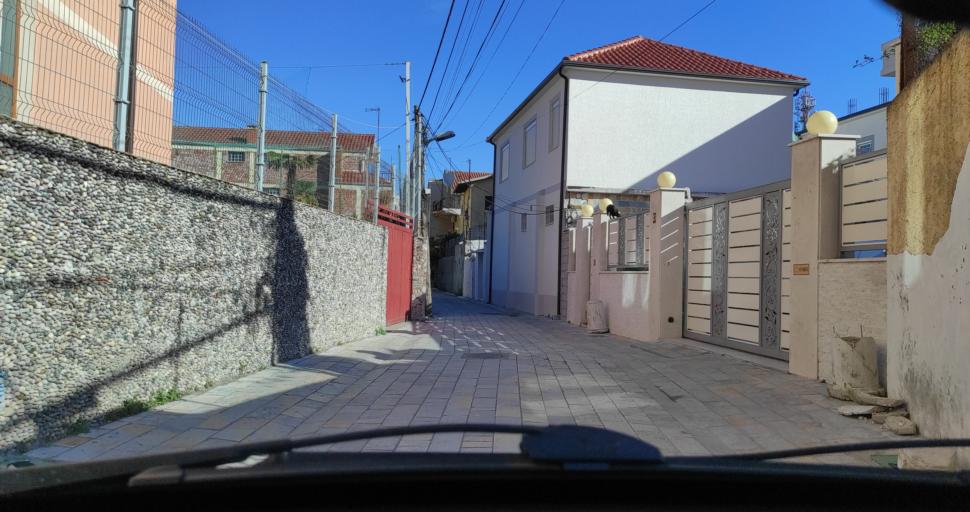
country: AL
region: Shkoder
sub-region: Rrethi i Shkodres
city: Shkoder
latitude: 42.0651
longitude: 19.5144
